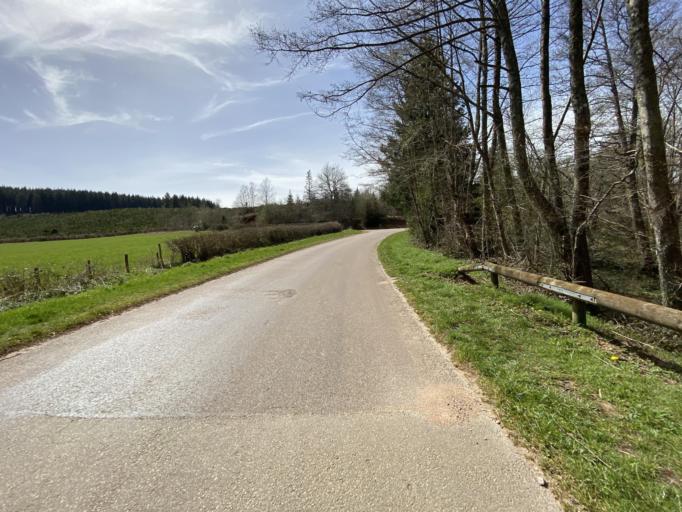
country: FR
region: Bourgogne
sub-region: Departement de la Cote-d'Or
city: Saulieu
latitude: 47.3179
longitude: 4.0976
